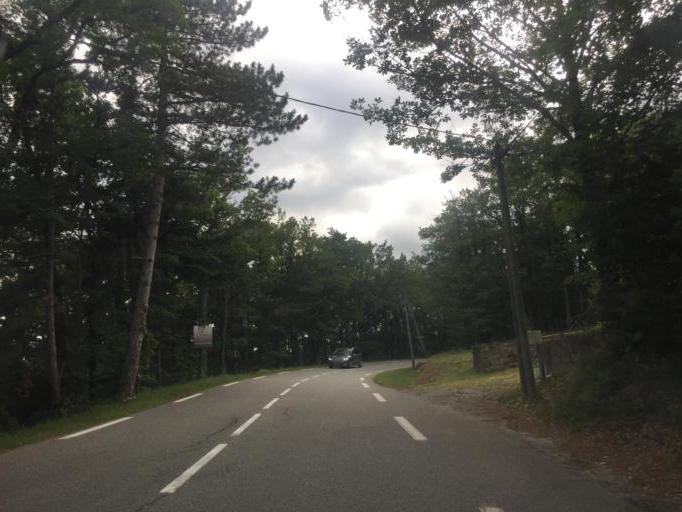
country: FR
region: Rhone-Alpes
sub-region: Departement de l'Ardeche
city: Veyras
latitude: 44.7534
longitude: 4.5816
